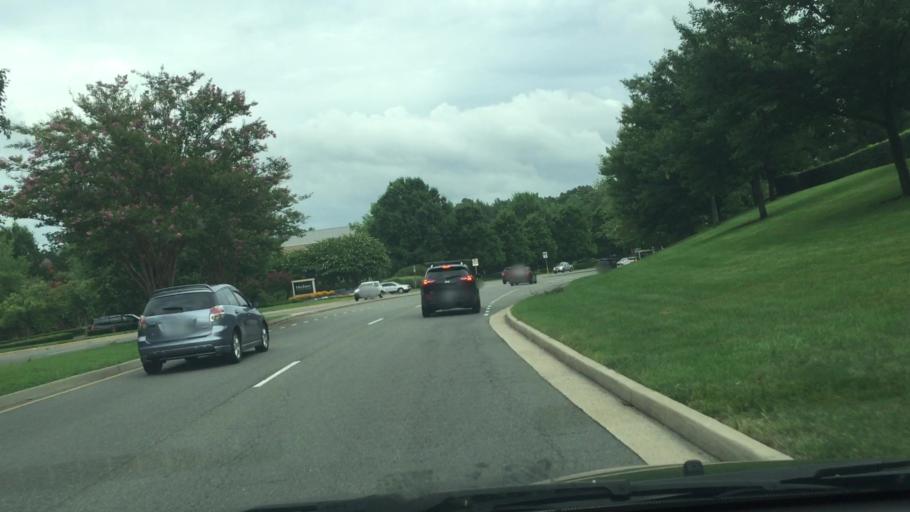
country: US
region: Virginia
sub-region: Henrico County
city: Tuckahoe
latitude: 37.6054
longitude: -77.5295
